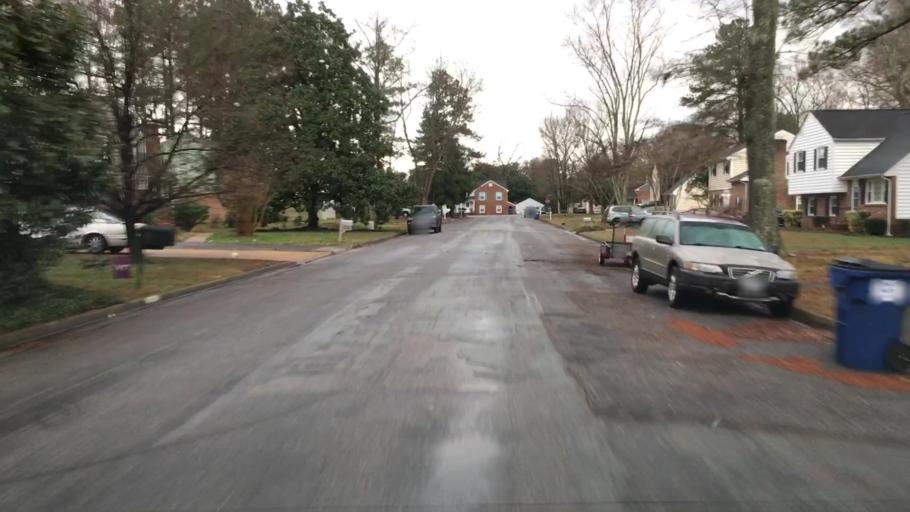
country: US
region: Virginia
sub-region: Chesterfield County
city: Bon Air
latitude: 37.5141
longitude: -77.6203
